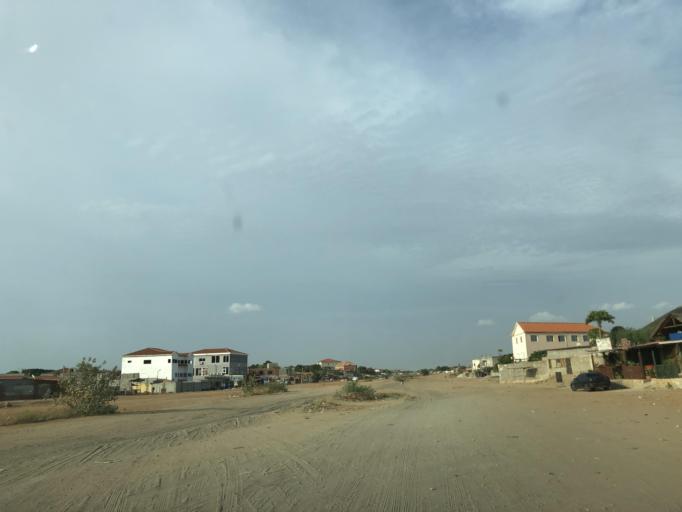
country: AO
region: Luanda
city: Luanda
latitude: -8.9261
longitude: 13.3047
